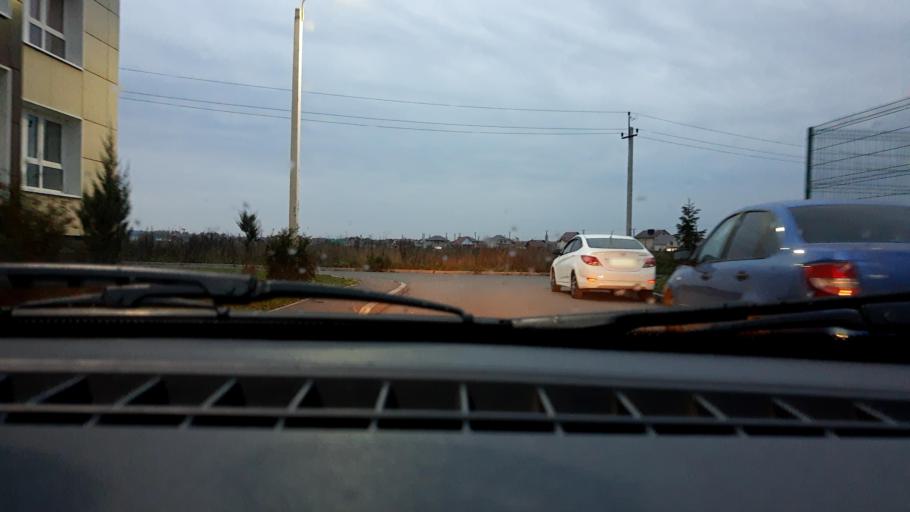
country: RU
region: Bashkortostan
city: Mikhaylovka
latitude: 54.7836
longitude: 55.8330
